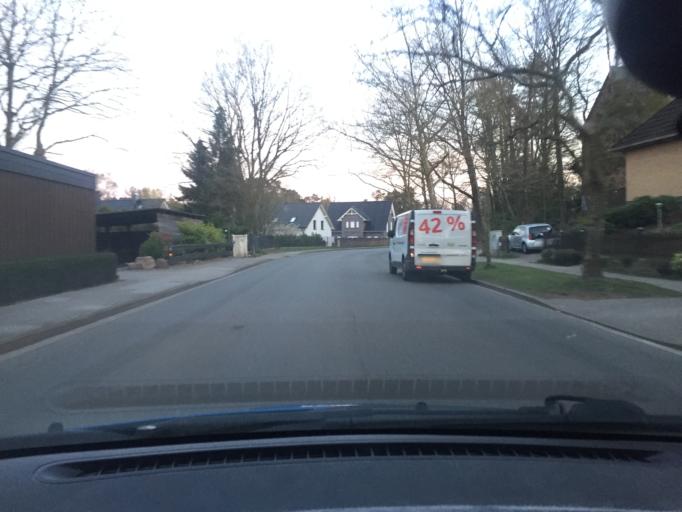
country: DE
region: Lower Saxony
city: Buchholz in der Nordheide
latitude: 53.3186
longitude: 9.8619
